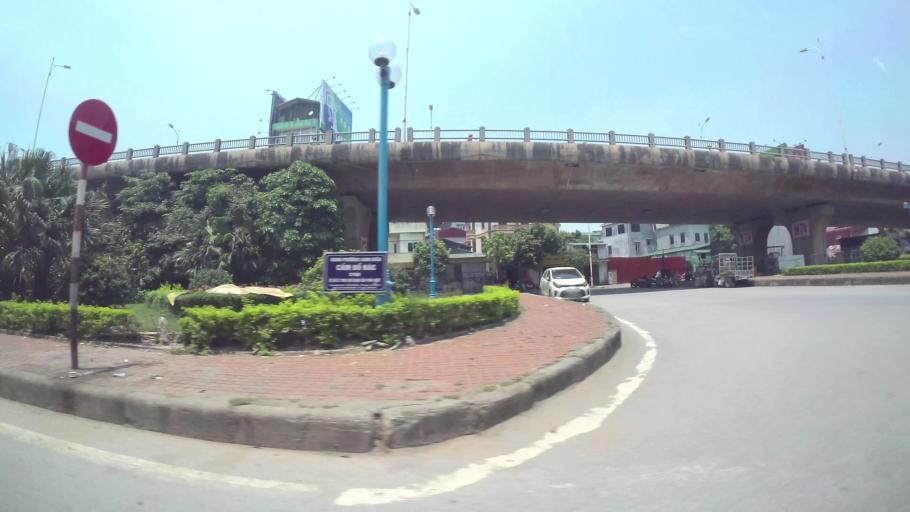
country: VN
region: Ha Noi
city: Trau Quy
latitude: 21.0229
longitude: 105.8942
